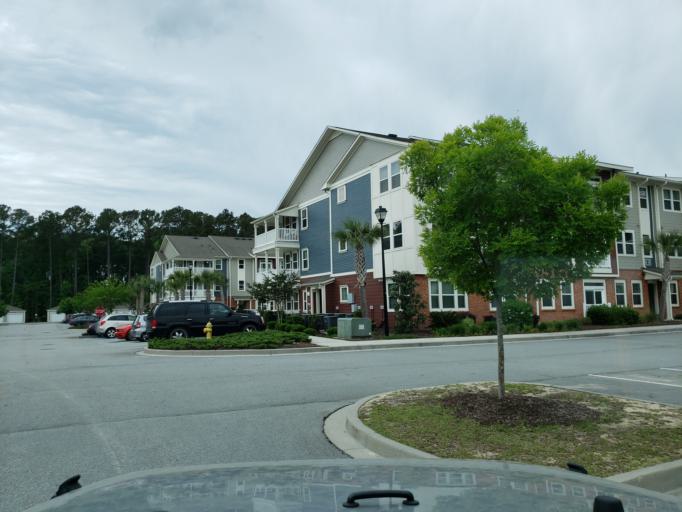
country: US
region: Georgia
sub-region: Chatham County
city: Pooler
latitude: 32.1751
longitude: -81.2303
